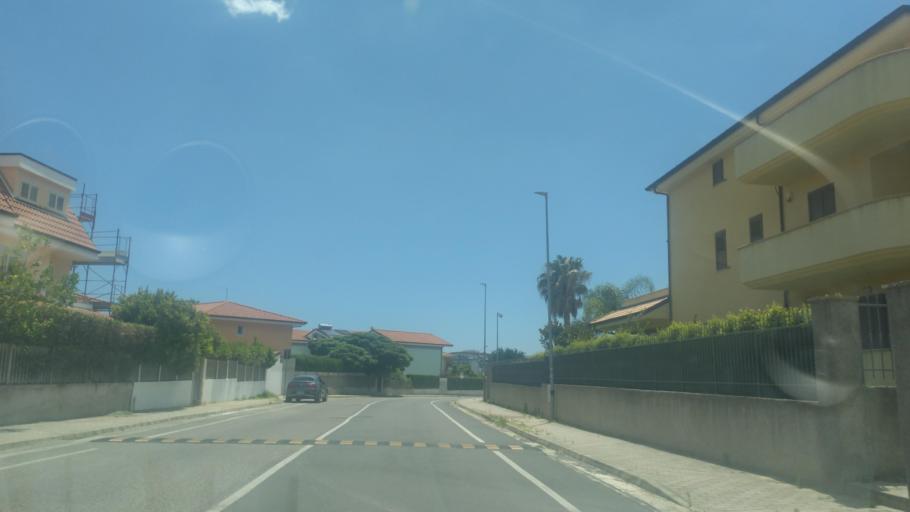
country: IT
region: Calabria
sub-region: Provincia di Catanzaro
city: Montepaone Lido
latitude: 38.7239
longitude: 16.5327
